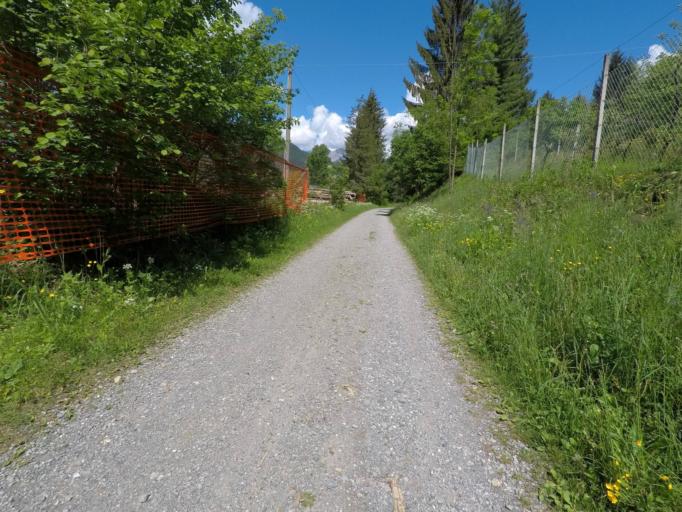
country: IT
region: Friuli Venezia Giulia
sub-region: Provincia di Udine
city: Ovaro
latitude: 46.4782
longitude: 12.8711
